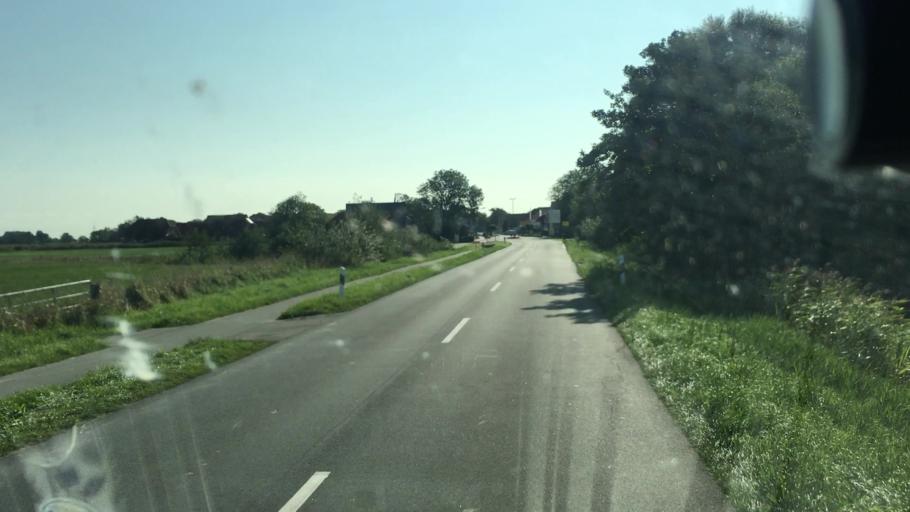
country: DE
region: Lower Saxony
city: Werdum
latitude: 53.6609
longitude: 7.7121
